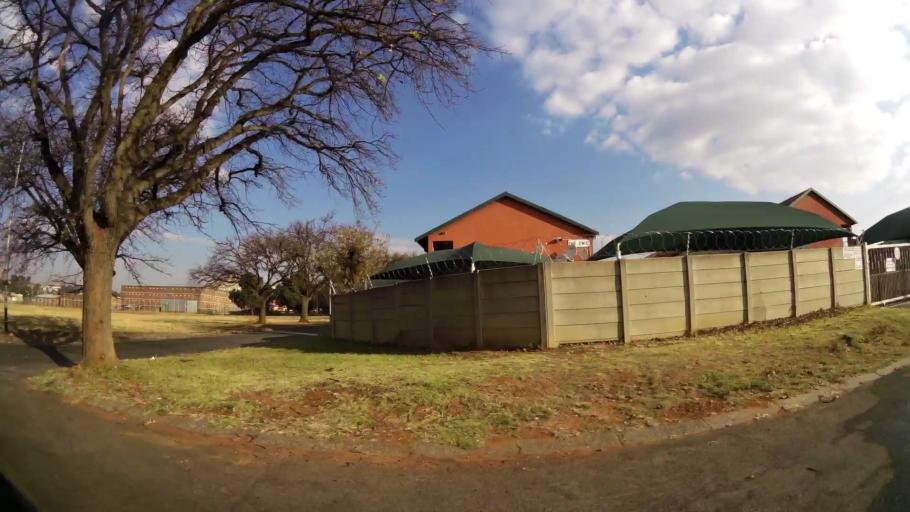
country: ZA
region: Gauteng
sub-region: West Rand District Municipality
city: Krugersdorp
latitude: -26.0991
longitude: 27.7619
